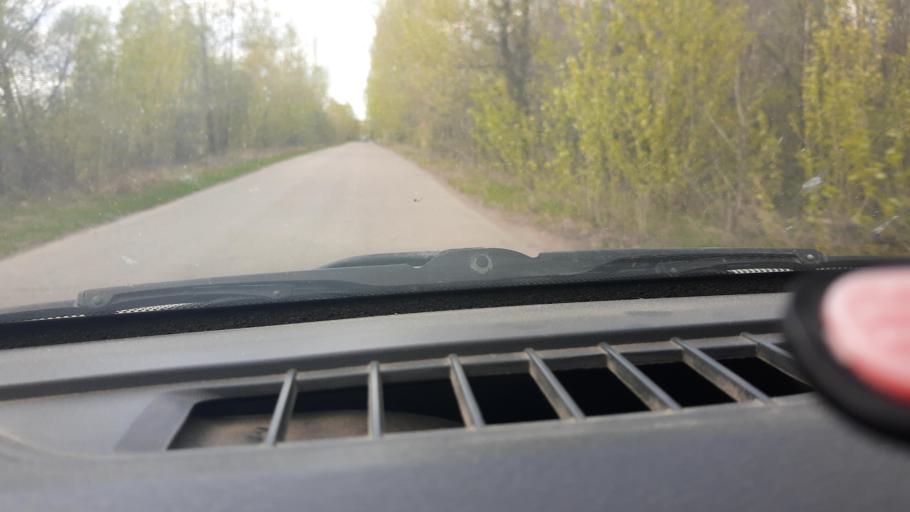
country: RU
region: Bashkortostan
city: Avdon
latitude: 54.6572
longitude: 55.8233
